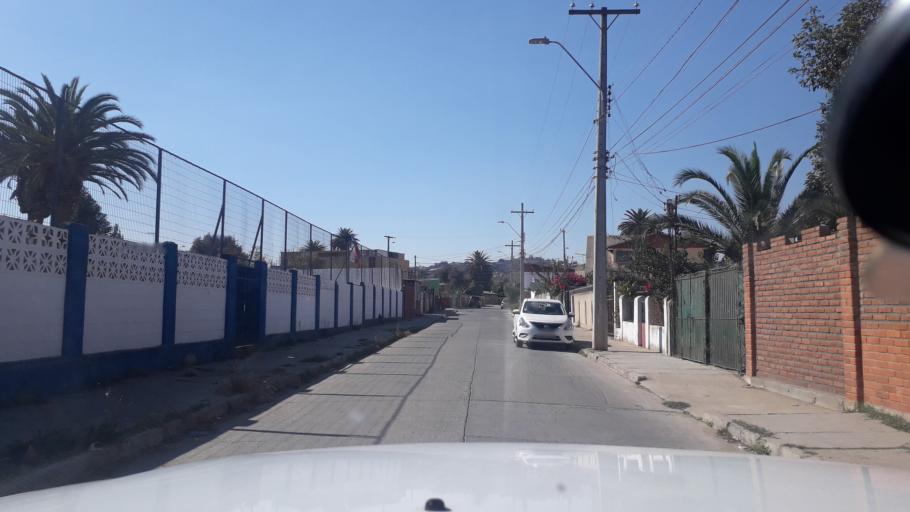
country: CL
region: Valparaiso
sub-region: Provincia de Marga Marga
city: Villa Alemana
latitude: -33.0400
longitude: -71.3548
